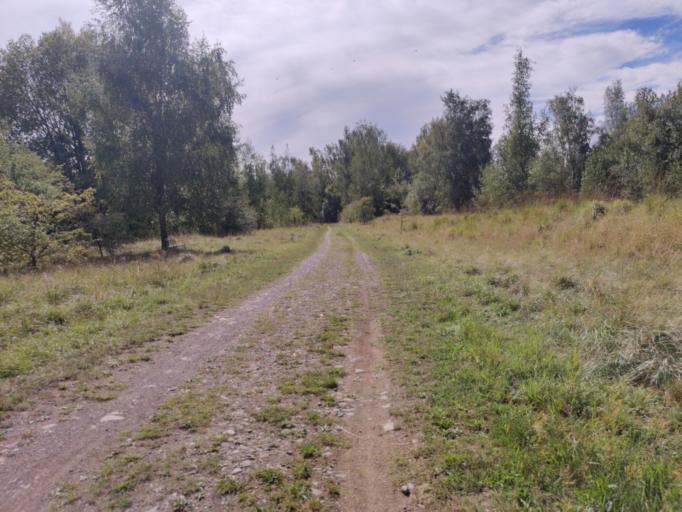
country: DE
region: Lower Saxony
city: Langelsheim
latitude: 51.9688
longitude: 10.3669
